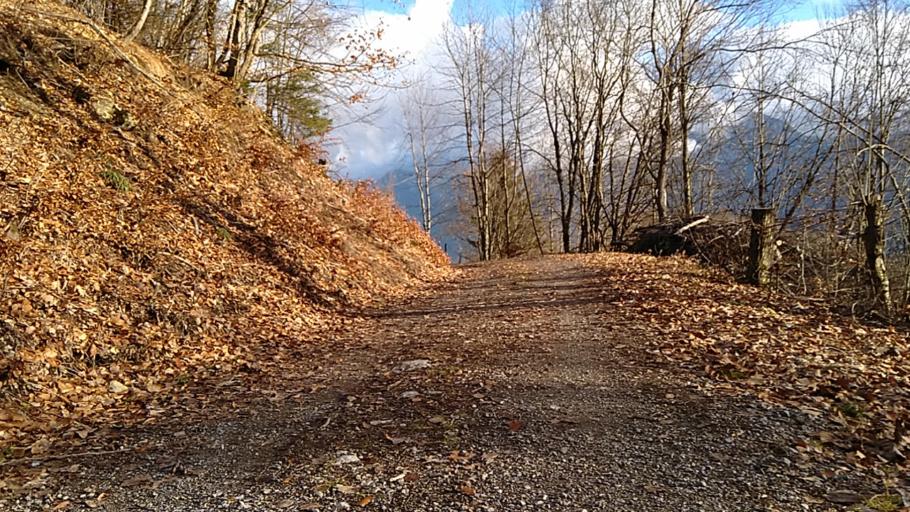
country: CH
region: Valais
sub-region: Monthey District
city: Vouvry
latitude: 46.3249
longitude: 6.8739
